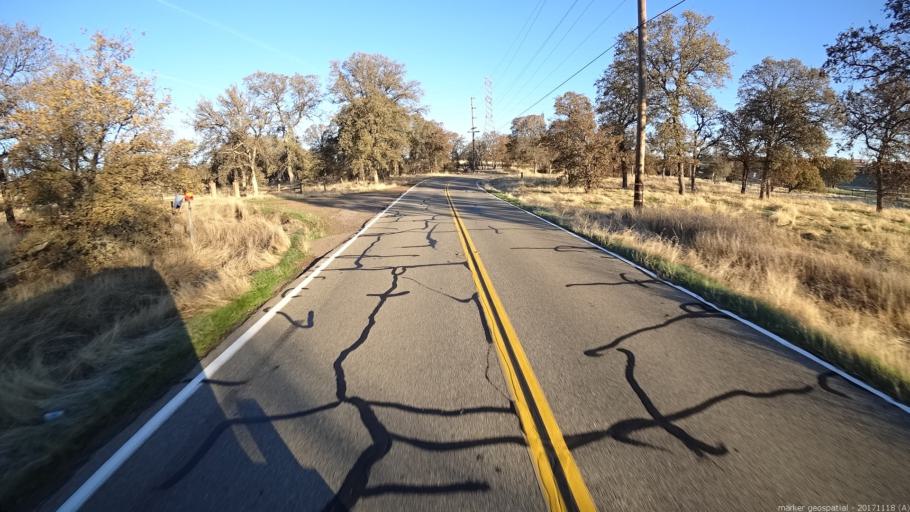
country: US
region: California
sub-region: Shasta County
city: Cottonwood
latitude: 40.4047
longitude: -122.2831
